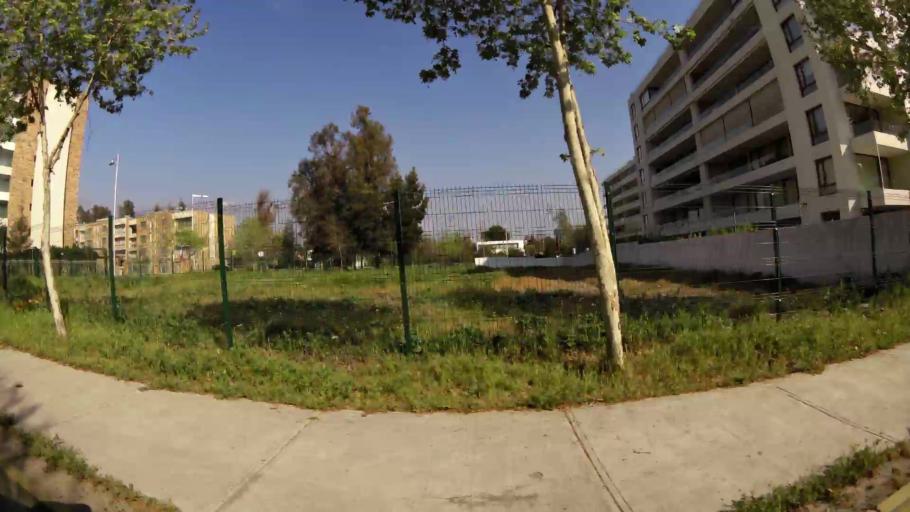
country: CL
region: Santiago Metropolitan
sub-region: Provincia de Santiago
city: Villa Presidente Frei, Nunoa, Santiago, Chile
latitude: -33.3770
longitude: -70.5553
